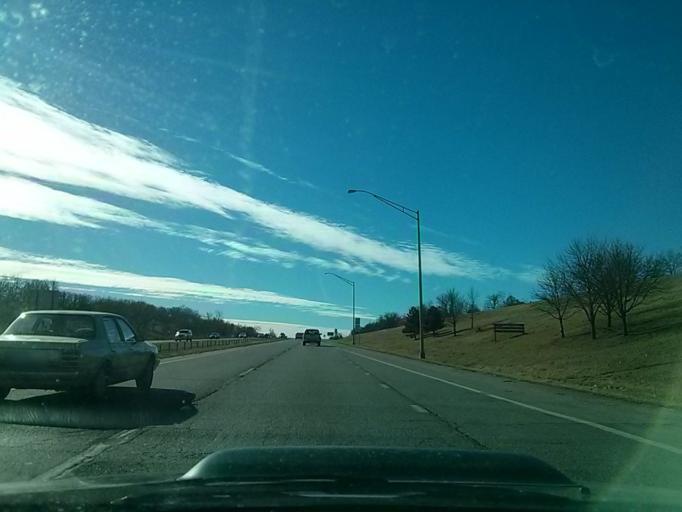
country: US
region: Oklahoma
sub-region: Tulsa County
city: Oakhurst
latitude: 36.0835
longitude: -96.0068
